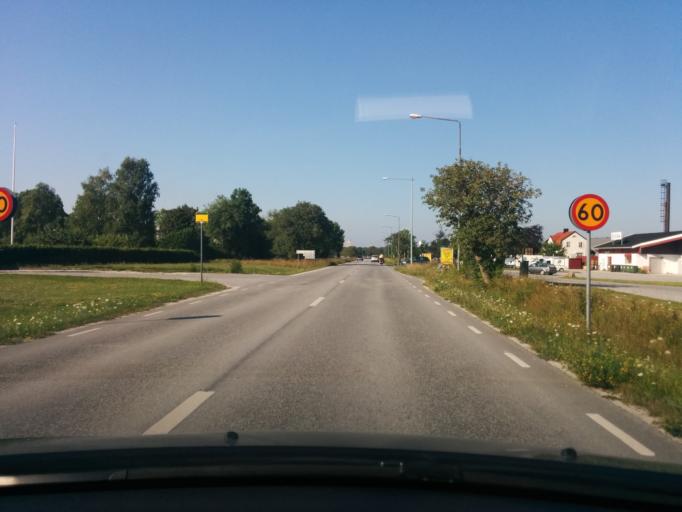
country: SE
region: Gotland
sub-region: Gotland
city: Slite
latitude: 57.6906
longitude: 18.7966
